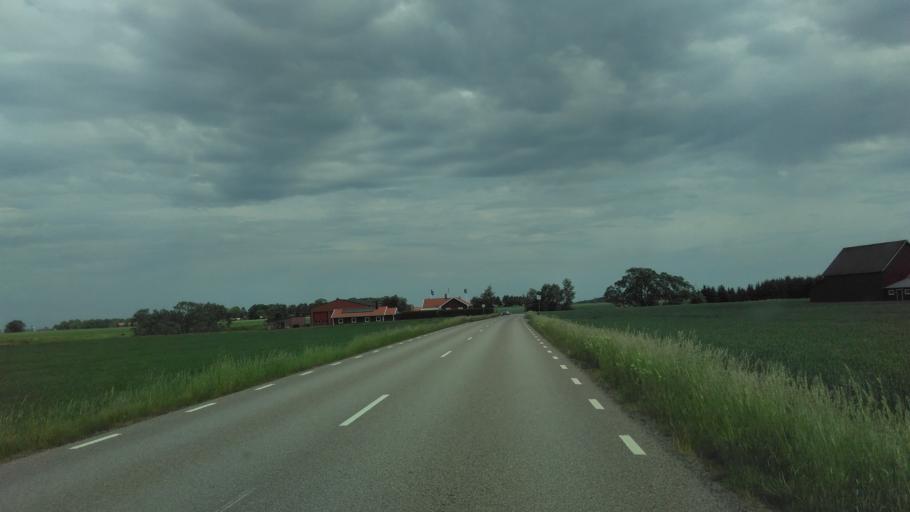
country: SE
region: Vaestra Goetaland
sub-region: Vara Kommun
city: Kvanum
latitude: 58.3618
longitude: 13.1422
